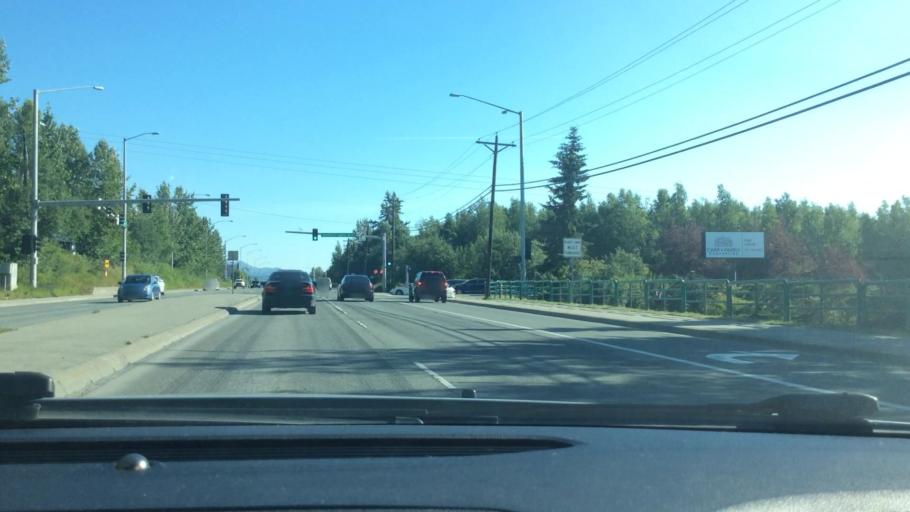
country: US
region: Alaska
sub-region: Anchorage Municipality
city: Elmendorf Air Force Base
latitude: 61.1960
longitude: -149.7335
